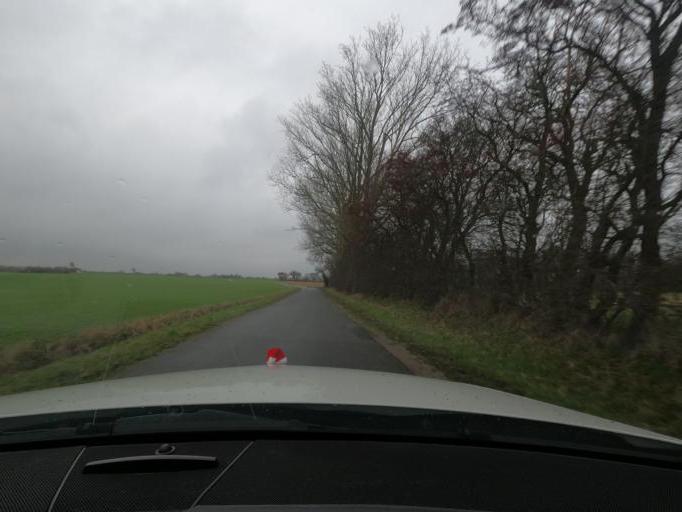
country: DK
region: South Denmark
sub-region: Haderslev Kommune
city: Starup
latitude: 55.2414
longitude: 9.6982
